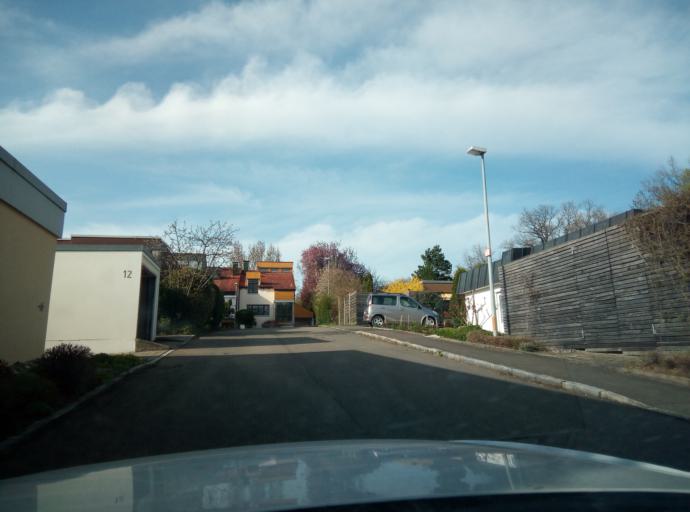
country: DE
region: Baden-Wuerttemberg
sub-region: Tuebingen Region
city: Tuebingen
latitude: 48.5435
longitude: 9.0659
